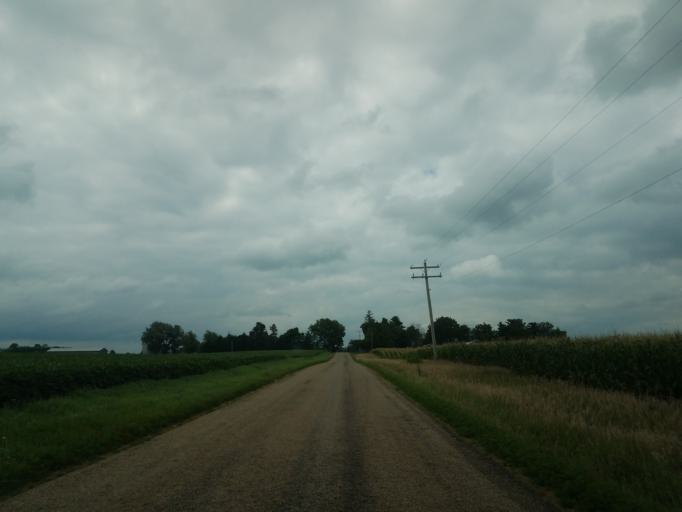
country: US
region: Illinois
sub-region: McLean County
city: Twin Grove
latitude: 40.4178
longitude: -89.0621
